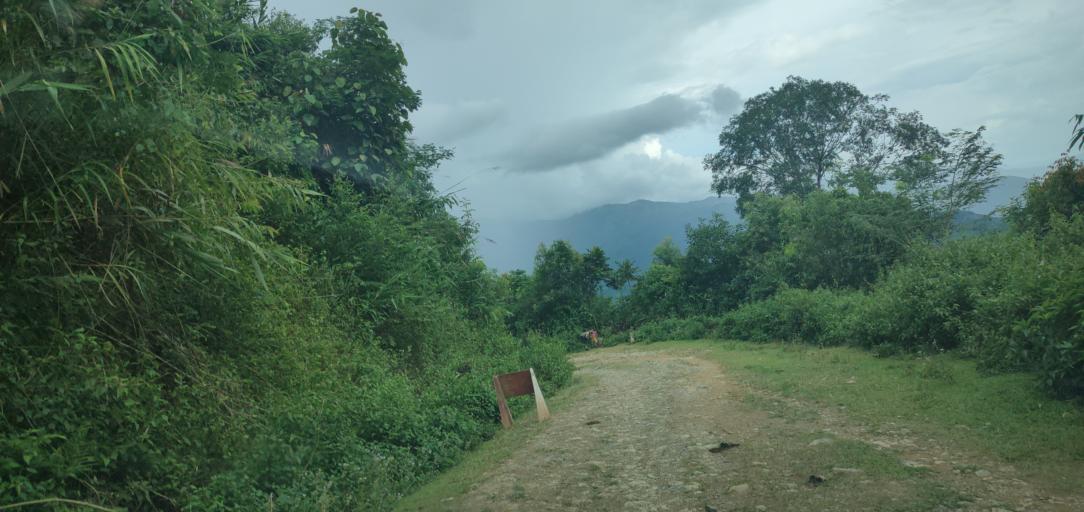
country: LA
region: Phongsali
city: Phongsali
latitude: 21.4462
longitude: 102.3030
